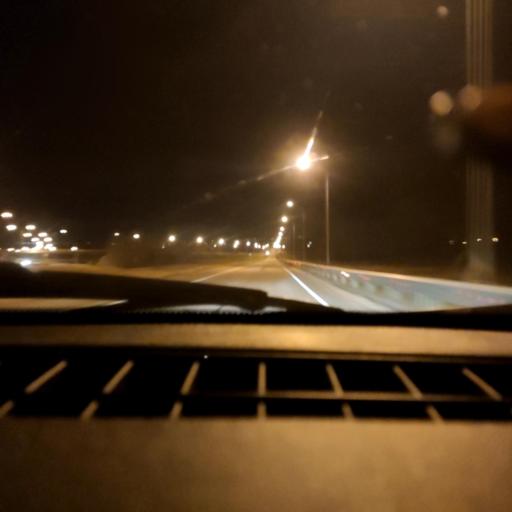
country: RU
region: Bashkortostan
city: Kushnarenkovo
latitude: 55.0577
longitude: 55.4305
